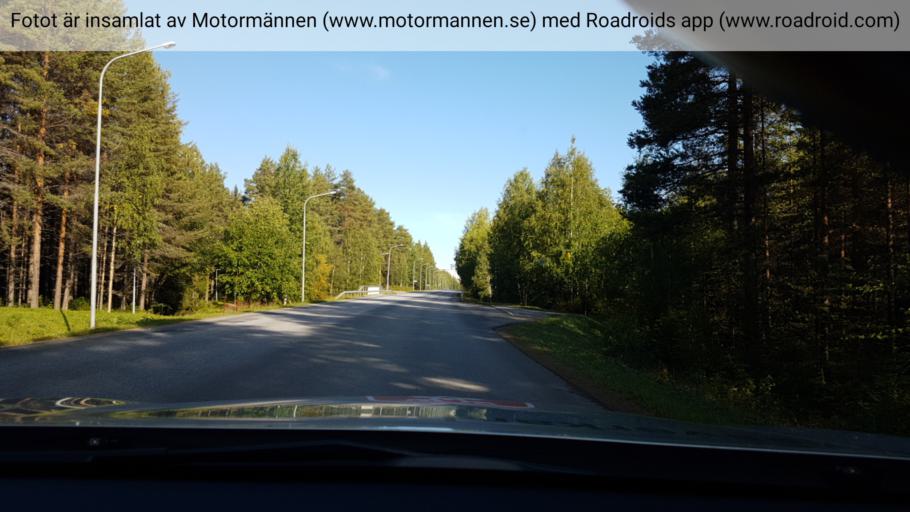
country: SE
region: Vaesterbotten
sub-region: Lycksele Kommun
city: Lycksele
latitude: 64.5743
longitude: 18.6857
